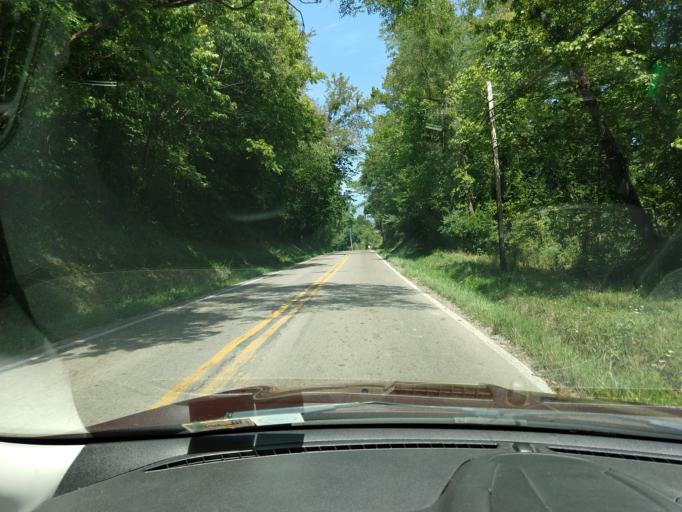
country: US
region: West Virginia
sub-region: Monongalia County
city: Westover
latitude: 39.6183
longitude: -79.9755
